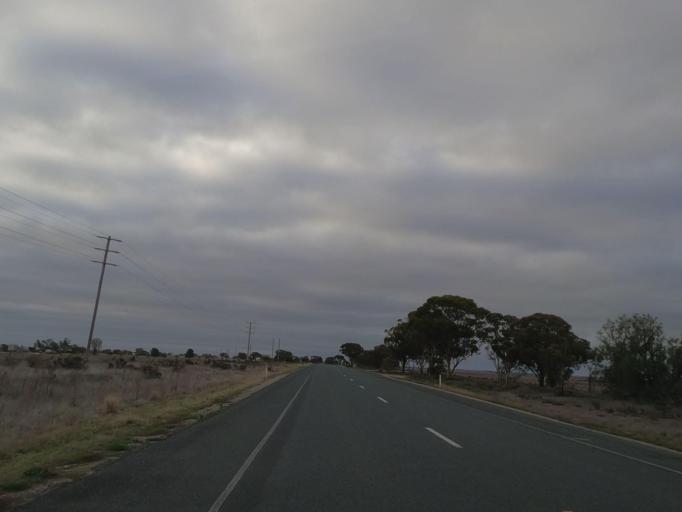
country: AU
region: Victoria
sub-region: Swan Hill
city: Swan Hill
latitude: -35.5875
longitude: 143.7903
